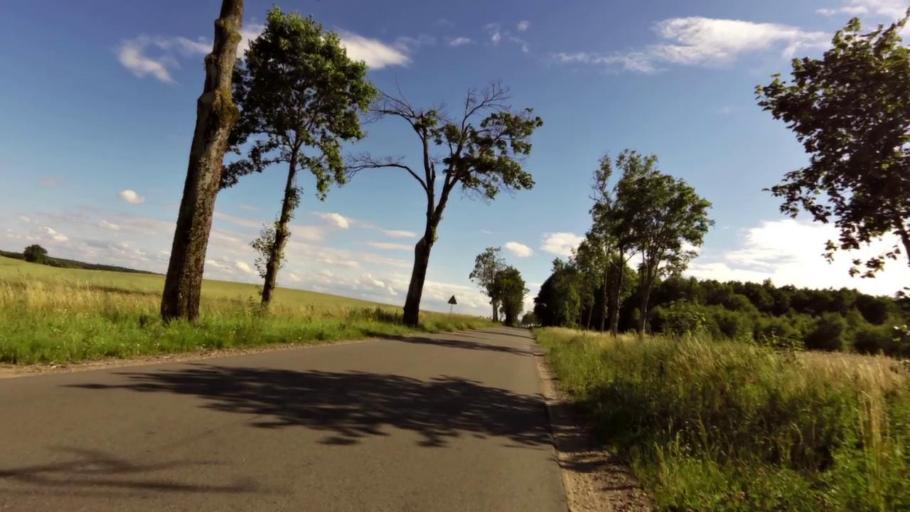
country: PL
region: West Pomeranian Voivodeship
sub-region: Powiat slawienski
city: Slawno
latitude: 54.4521
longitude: 16.7385
